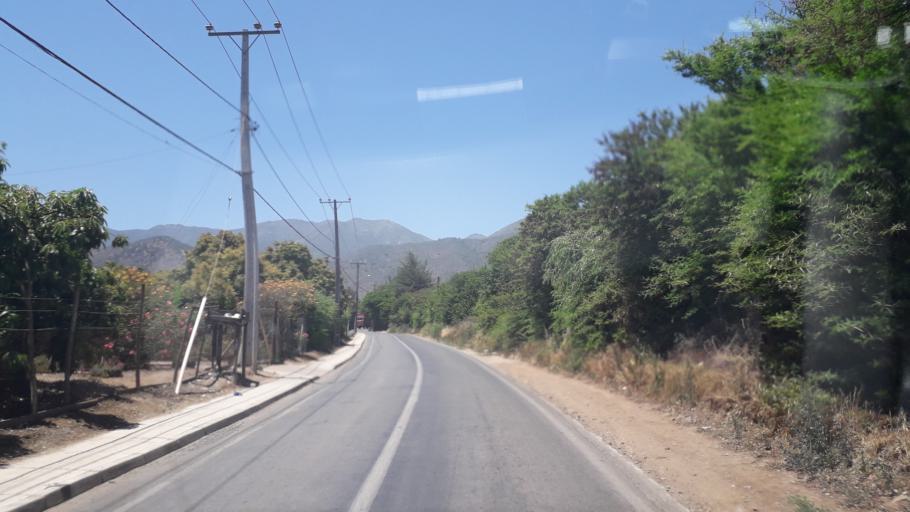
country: CL
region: Valparaiso
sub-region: Provincia de Quillota
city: Quillota
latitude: -32.9077
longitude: -71.2158
